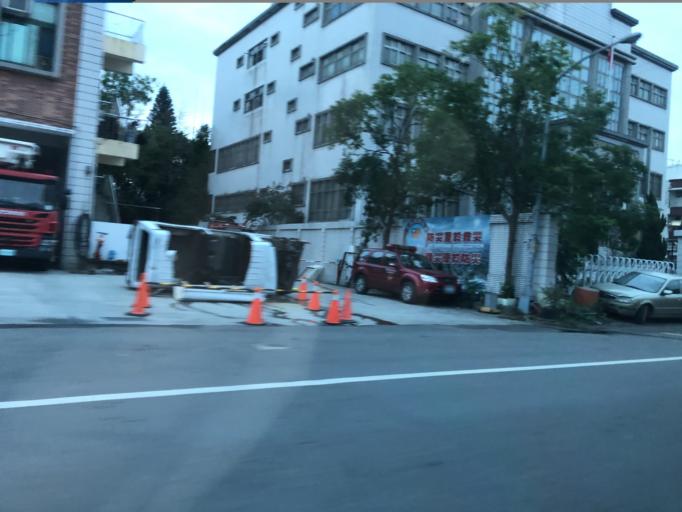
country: TW
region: Taiwan
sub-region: Hsinchu
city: Zhubei
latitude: 24.7355
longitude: 121.0929
